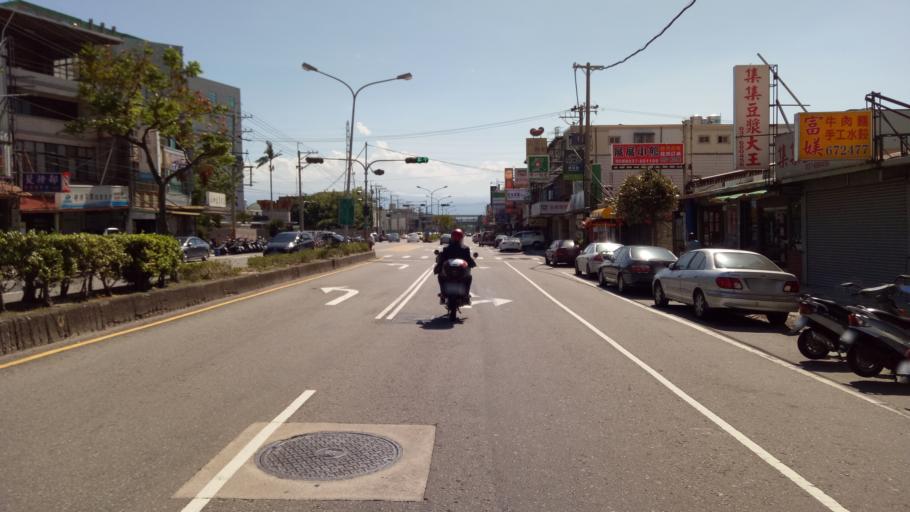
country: TW
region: Taiwan
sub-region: Hsinchu
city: Hsinchu
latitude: 24.7101
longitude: 120.9238
